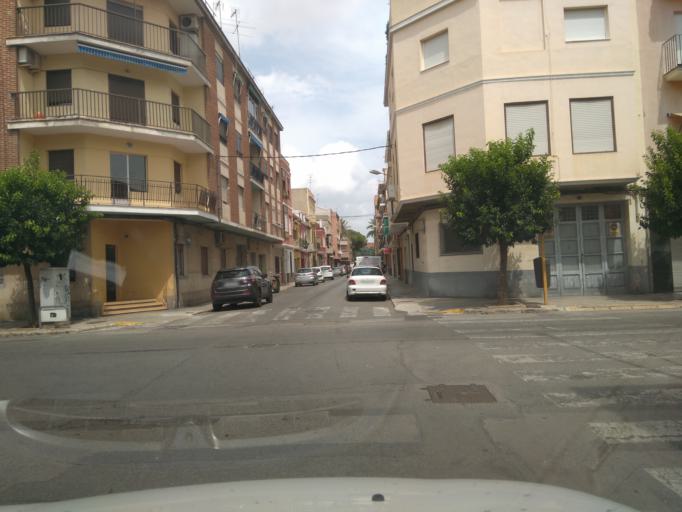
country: ES
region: Valencia
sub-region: Provincia de Valencia
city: Carcaixent
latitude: 39.1240
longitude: -0.4467
